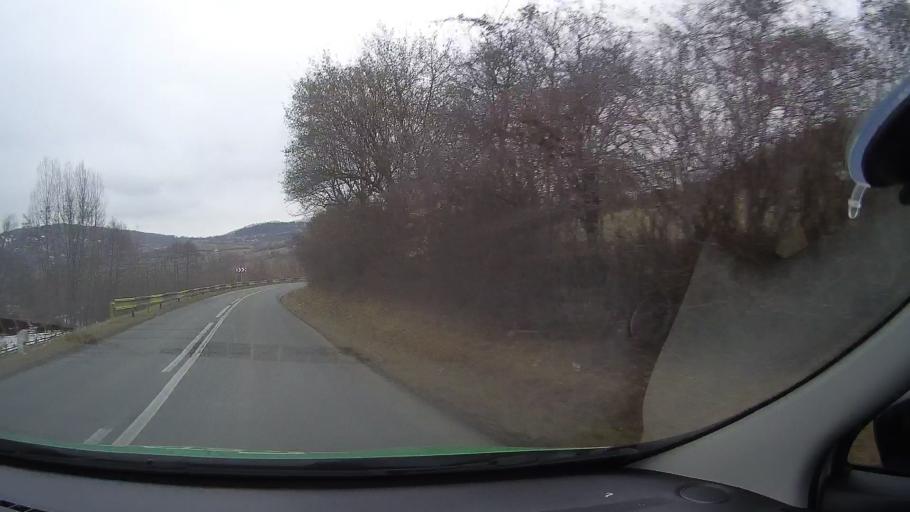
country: RO
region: Alba
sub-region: Comuna Metes
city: Metes
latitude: 46.1070
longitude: 23.4497
